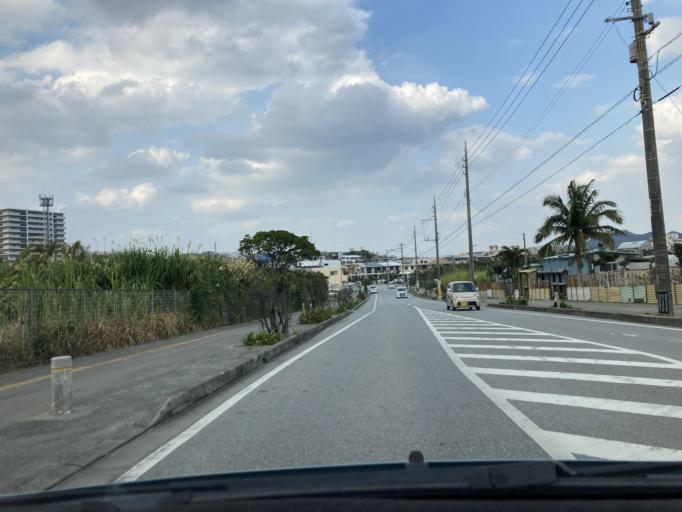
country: JP
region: Okinawa
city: Tomigusuku
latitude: 26.1930
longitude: 127.7331
